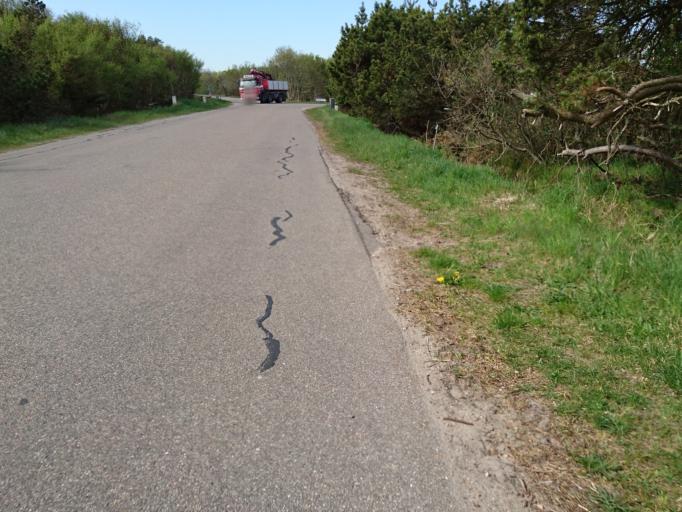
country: DK
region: North Denmark
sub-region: Frederikshavn Kommune
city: Skagen
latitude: 57.7200
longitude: 10.5433
